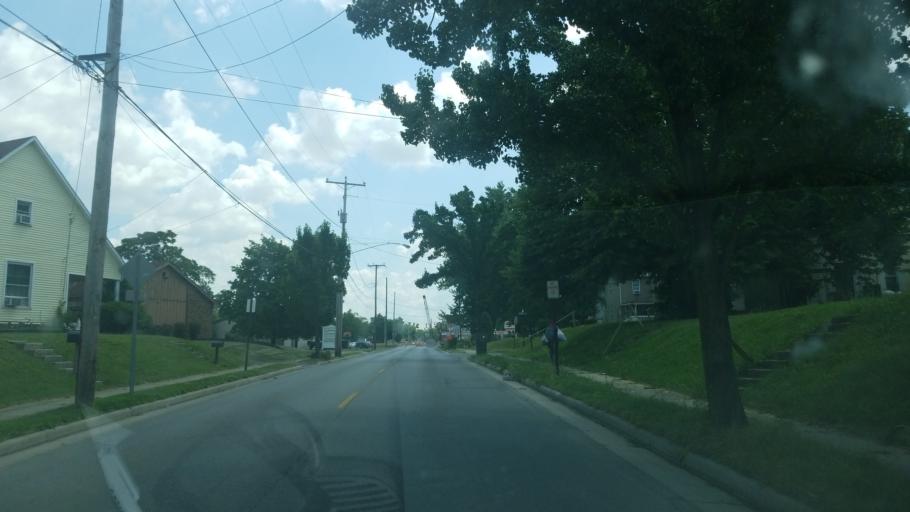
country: US
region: Ohio
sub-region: Allen County
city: Lima
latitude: 40.7377
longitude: -84.0935
